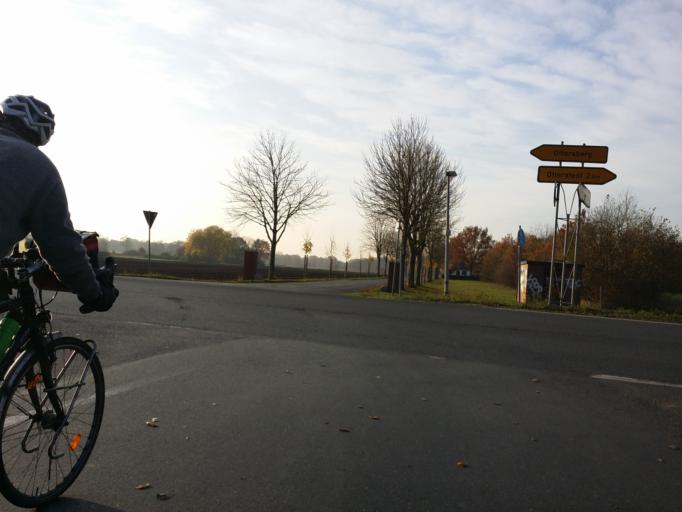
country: DE
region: Lower Saxony
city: Ottersberg
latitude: 53.1203
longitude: 9.1421
